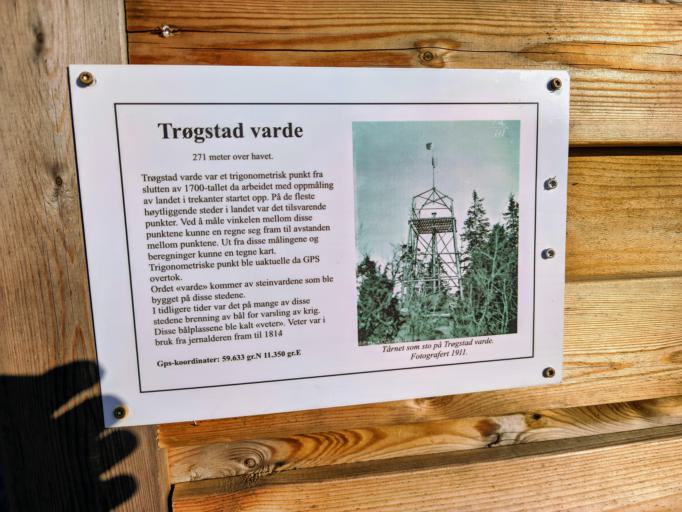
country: NO
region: Ostfold
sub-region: Trogstad
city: Skjonhaug
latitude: 59.6335
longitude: 11.3412
